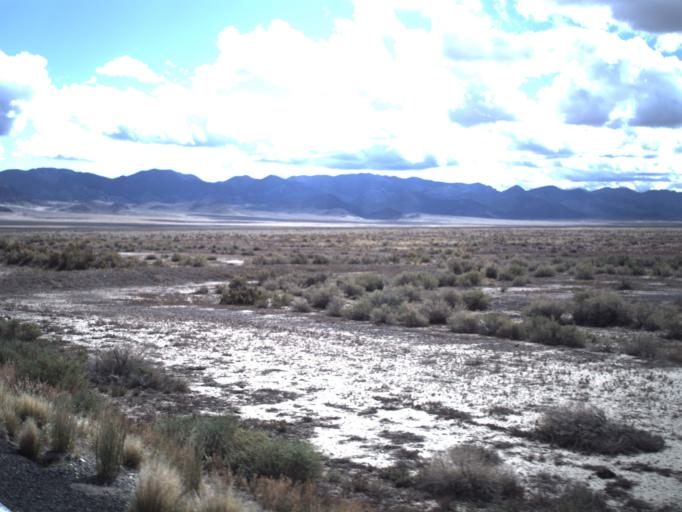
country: US
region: Utah
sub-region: Beaver County
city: Milford
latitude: 38.5314
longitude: -113.6794
